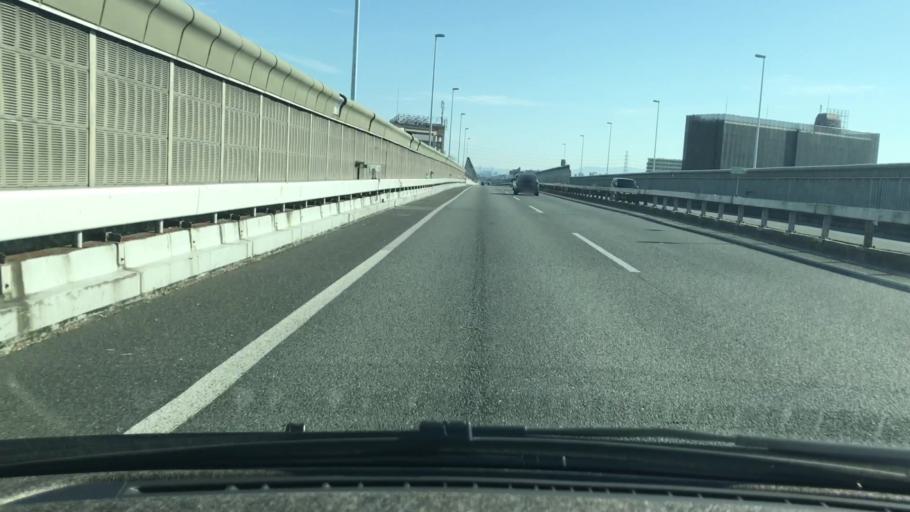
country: JP
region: Hyogo
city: Itami
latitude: 34.7448
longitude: 135.3767
